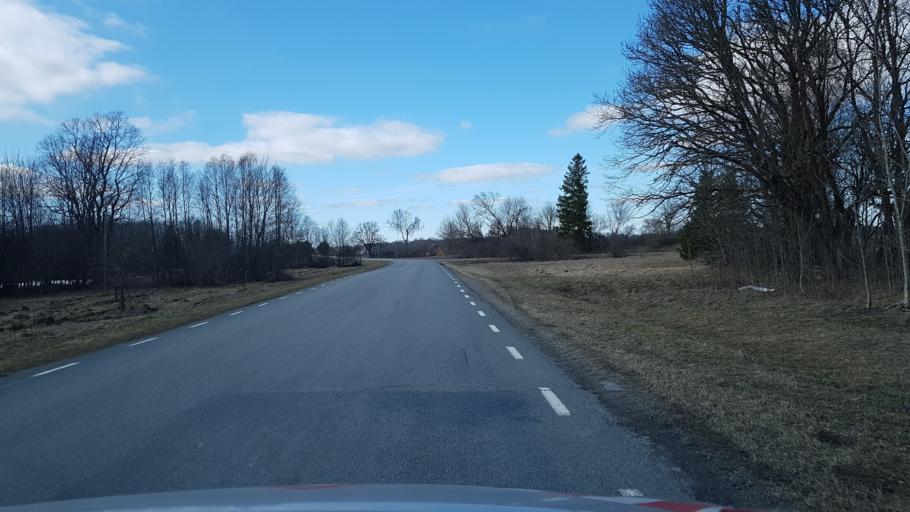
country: EE
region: Laeaene-Virumaa
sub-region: Tamsalu vald
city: Tamsalu
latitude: 59.1798
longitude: 26.0513
